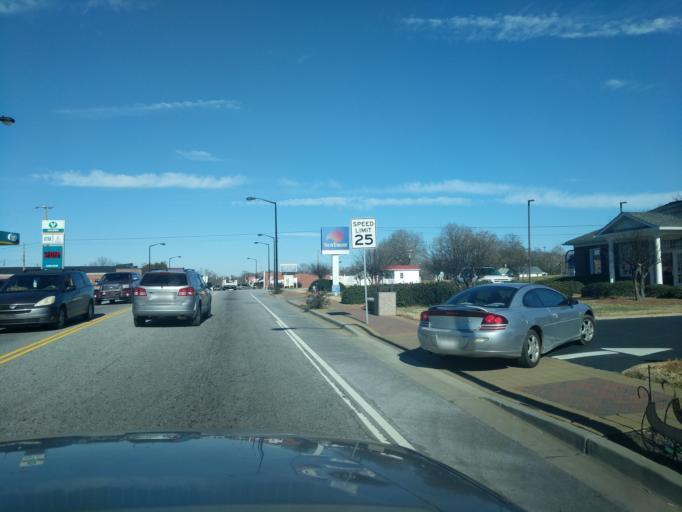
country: US
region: South Carolina
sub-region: Spartanburg County
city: Mayo
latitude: 35.1448
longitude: -81.8604
